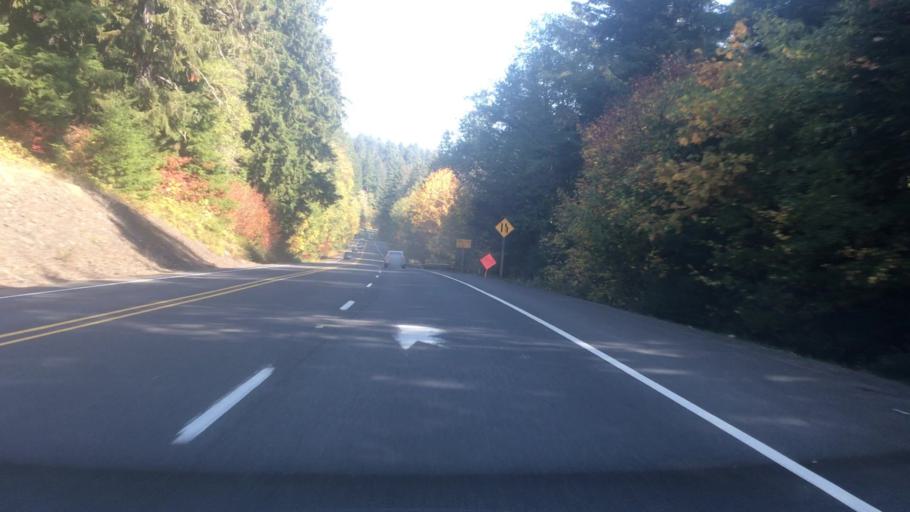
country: US
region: Oregon
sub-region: Lincoln County
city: Rose Lodge
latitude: 45.0495
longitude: -123.7848
